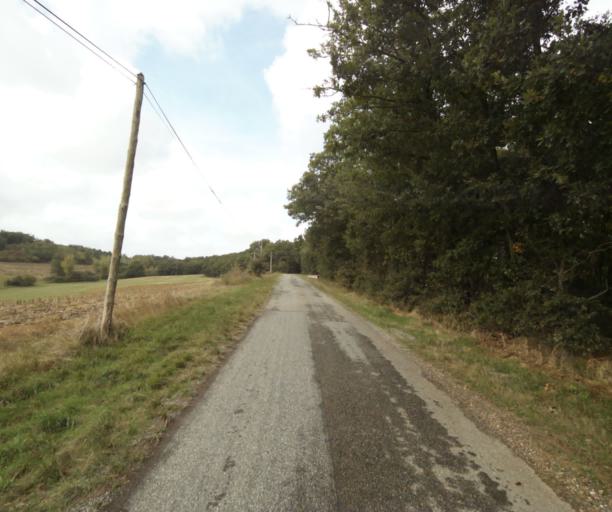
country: FR
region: Midi-Pyrenees
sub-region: Departement du Tarn-et-Garonne
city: Beaumont-de-Lomagne
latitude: 43.8685
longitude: 1.1050
